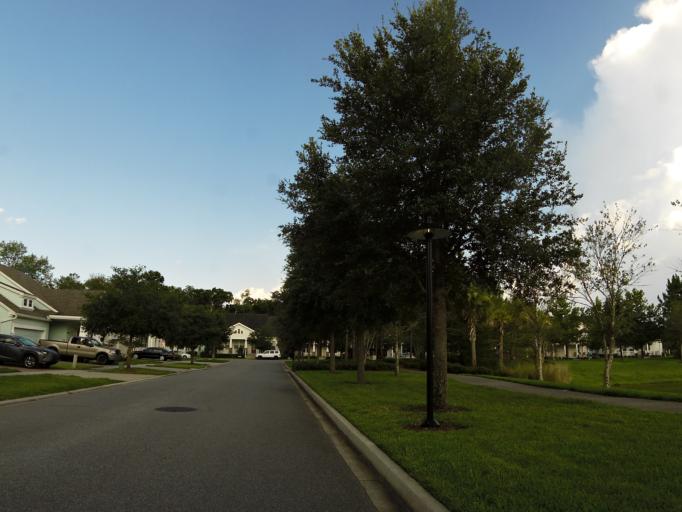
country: US
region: Florida
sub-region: Clay County
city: Green Cove Springs
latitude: 30.0249
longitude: -81.6345
